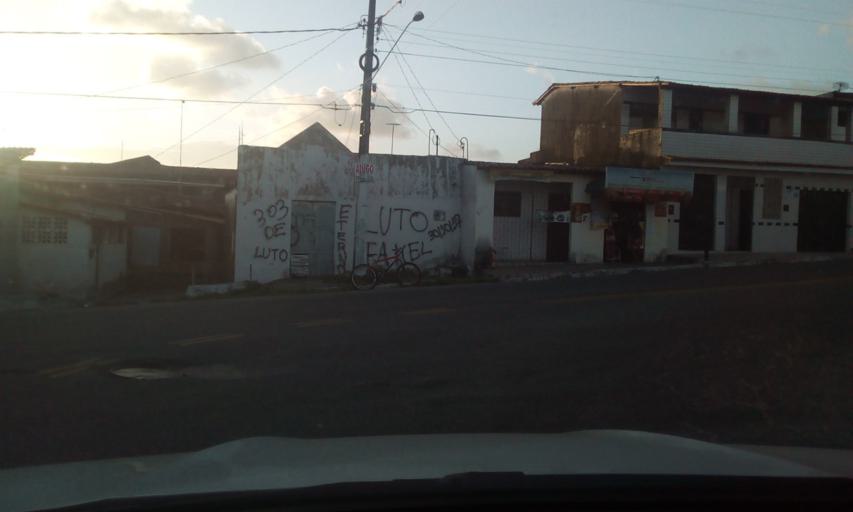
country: BR
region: Paraiba
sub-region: Joao Pessoa
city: Joao Pessoa
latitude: -7.1869
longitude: -34.8472
